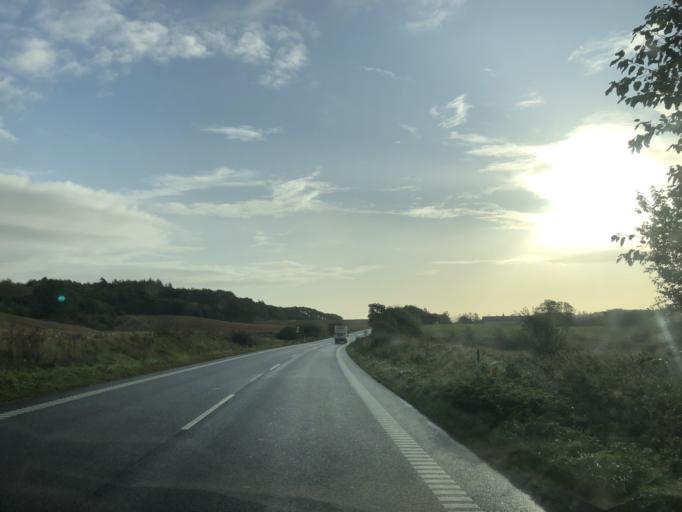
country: DK
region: North Denmark
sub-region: Mariagerfjord Kommune
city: Hobro
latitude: 56.6156
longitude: 9.6706
